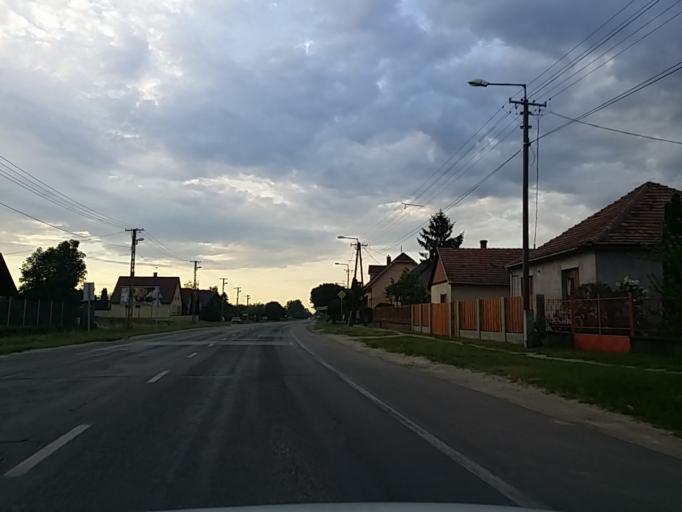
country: HU
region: Bacs-Kiskun
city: Lajosmizse
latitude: 47.0182
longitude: 19.5701
